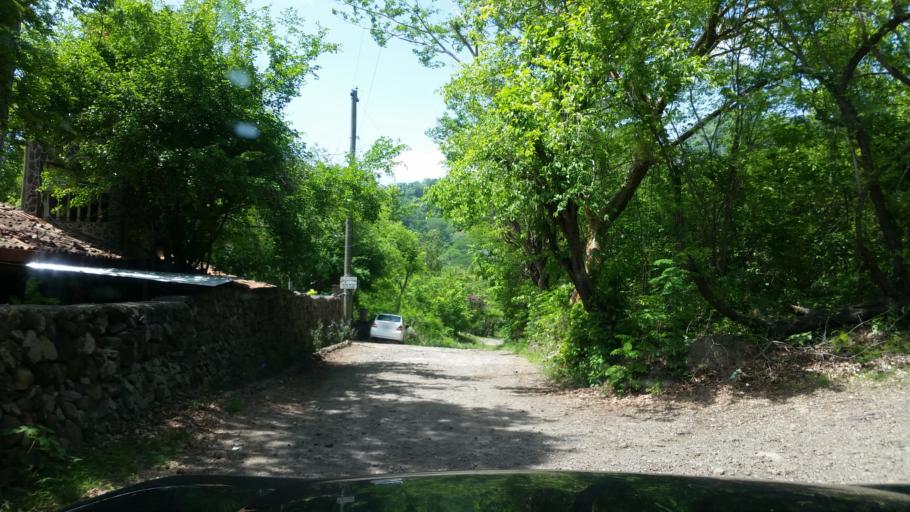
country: NI
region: Masaya
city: Catarina
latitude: 11.9111
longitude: -86.0558
